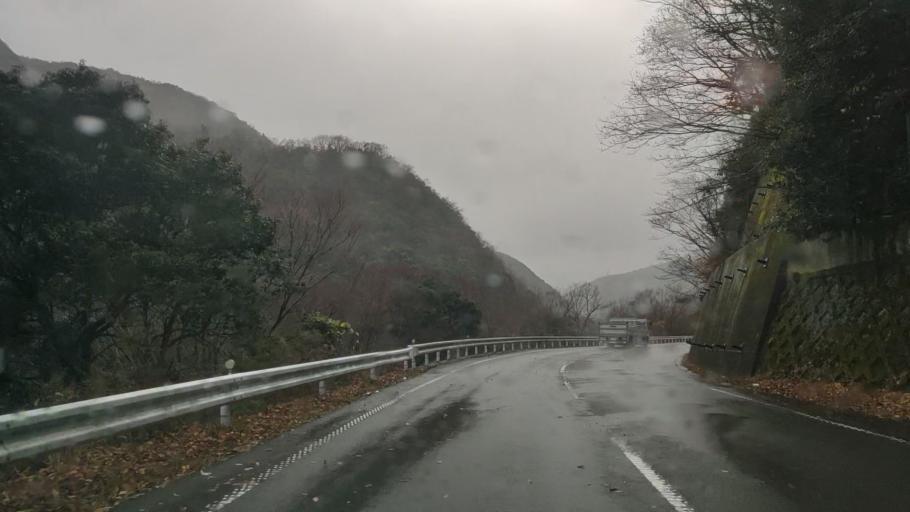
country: JP
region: Tokushima
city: Kamojimacho-jogejima
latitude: 34.1449
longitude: 134.3538
